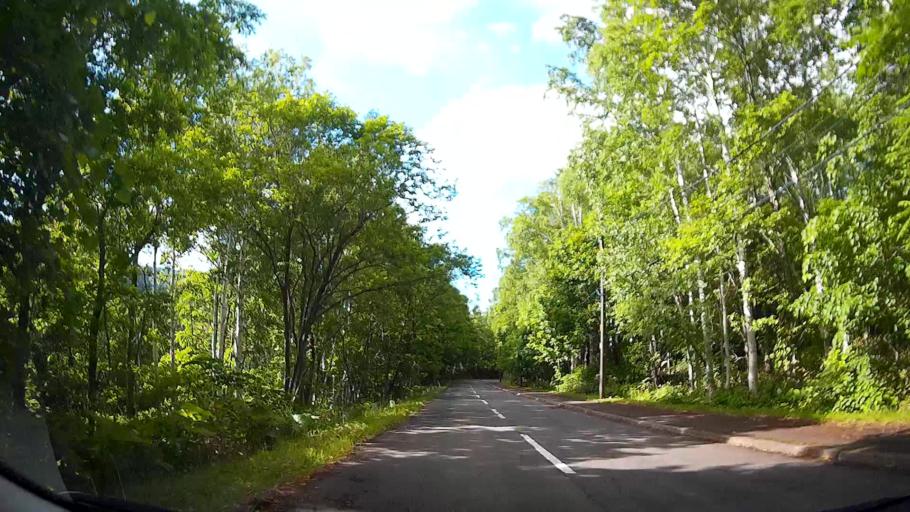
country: JP
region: Hokkaido
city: Sapporo
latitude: 42.9357
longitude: 141.1530
